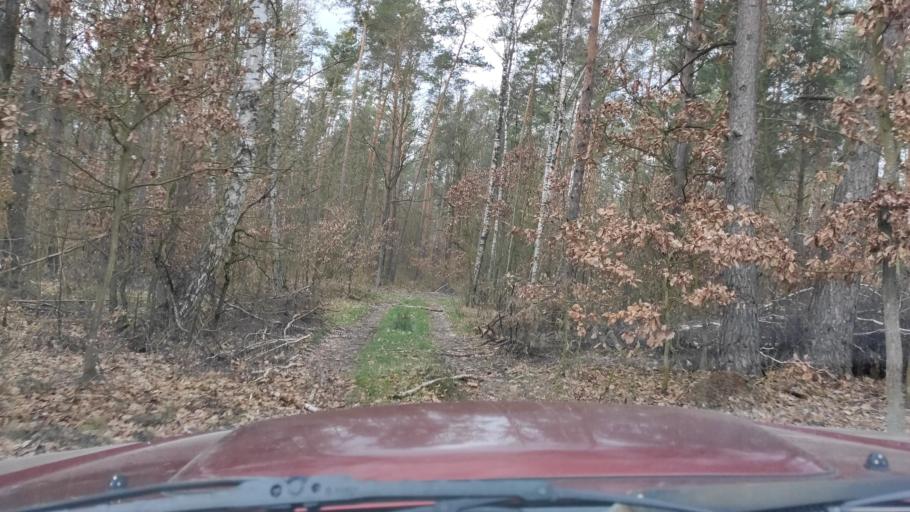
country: PL
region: Masovian Voivodeship
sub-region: Powiat kozienicki
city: Garbatka-Letnisko
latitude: 51.5144
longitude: 21.5656
